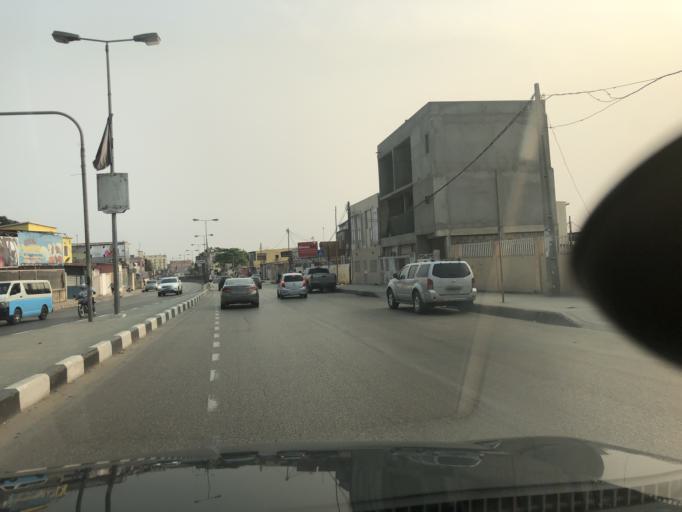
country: AO
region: Luanda
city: Luanda
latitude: -8.8370
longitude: 13.2150
